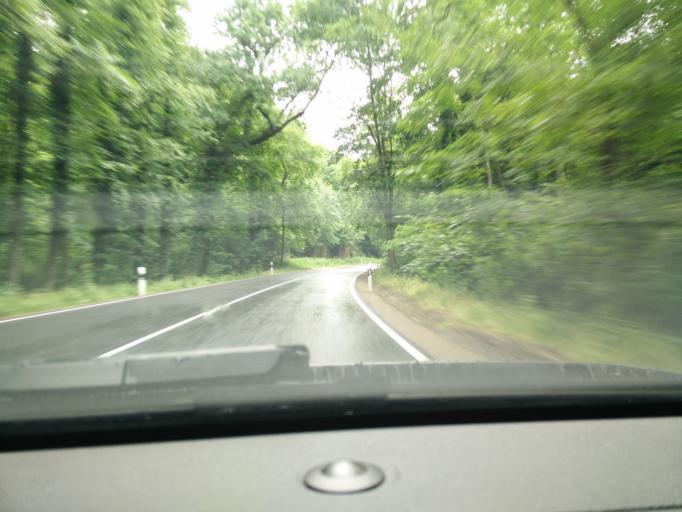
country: DE
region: Saxony
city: Nerchau
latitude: 51.2419
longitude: 12.7626
